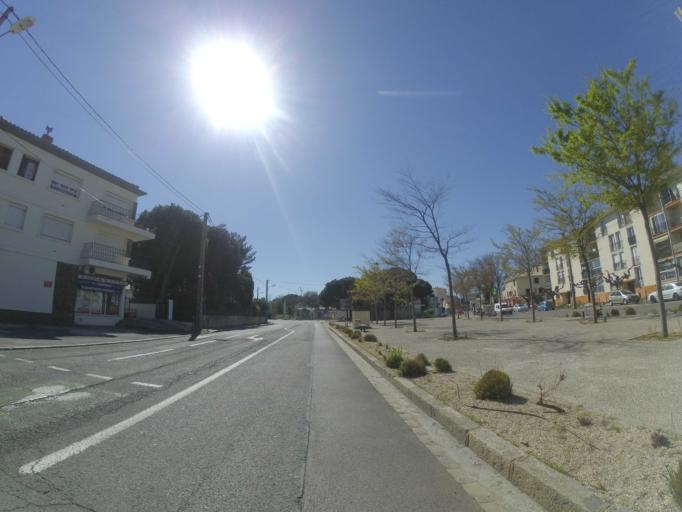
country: FR
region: Languedoc-Roussillon
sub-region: Departement des Pyrenees-Orientales
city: Perpignan
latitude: 42.7190
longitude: 2.8900
